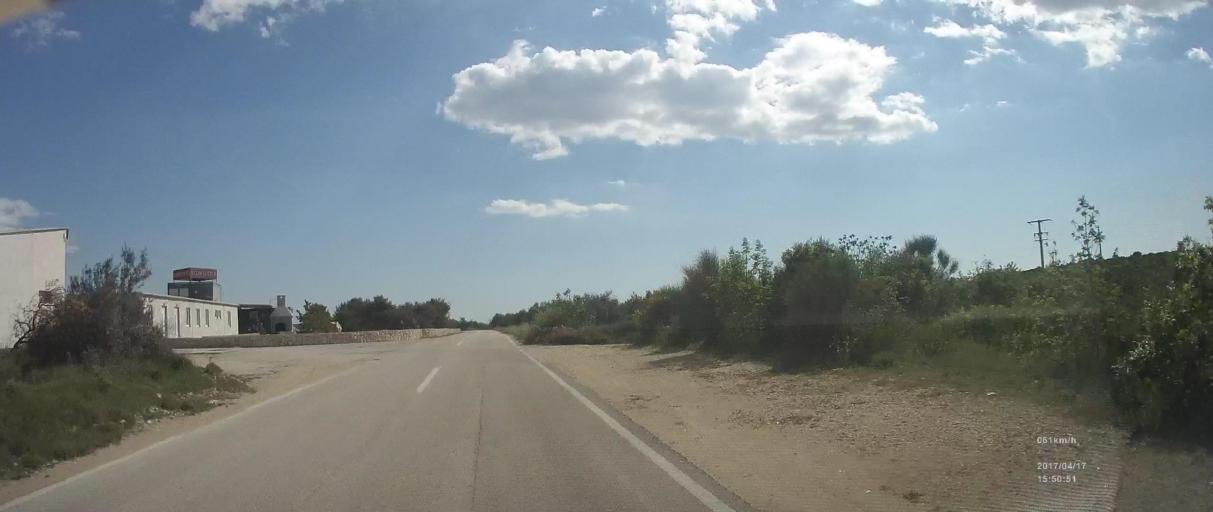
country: HR
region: Sibensko-Kniniska
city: Primosten
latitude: 43.6056
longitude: 15.9696
